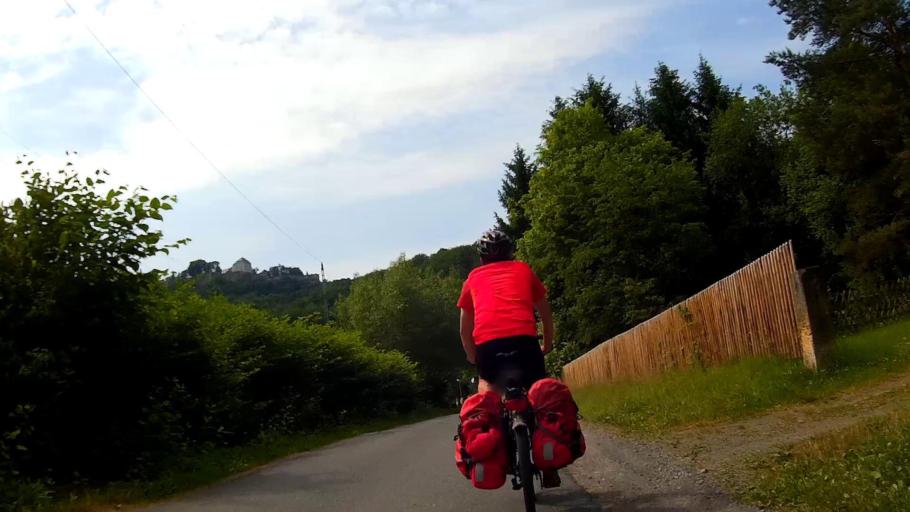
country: DE
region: Saxony
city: Konigstein
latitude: 50.9300
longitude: 14.0556
